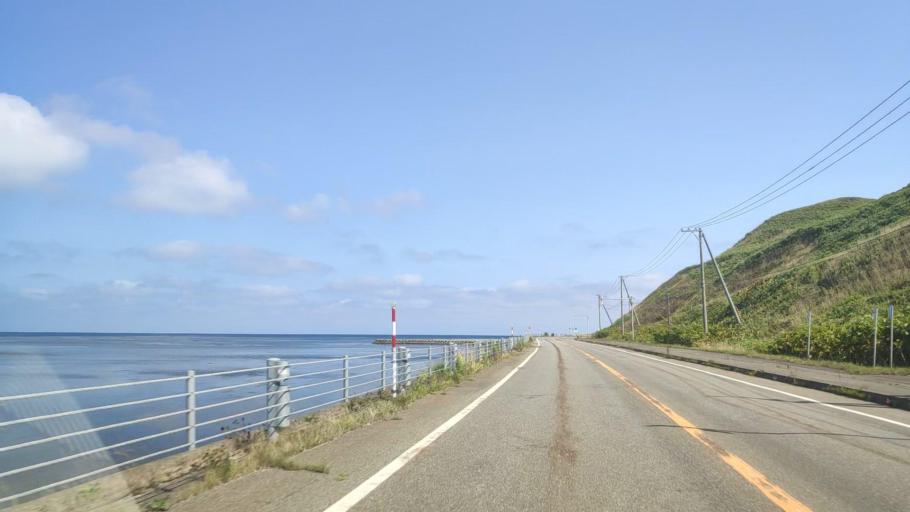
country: JP
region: Hokkaido
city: Makubetsu
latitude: 45.4925
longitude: 141.8793
